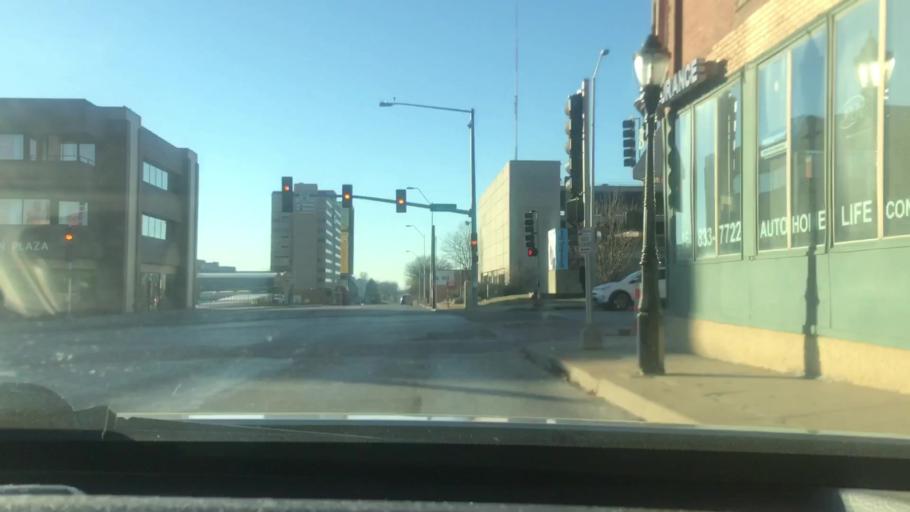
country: US
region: Missouri
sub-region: Jackson County
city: Kansas City
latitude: 39.0711
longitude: -94.5850
